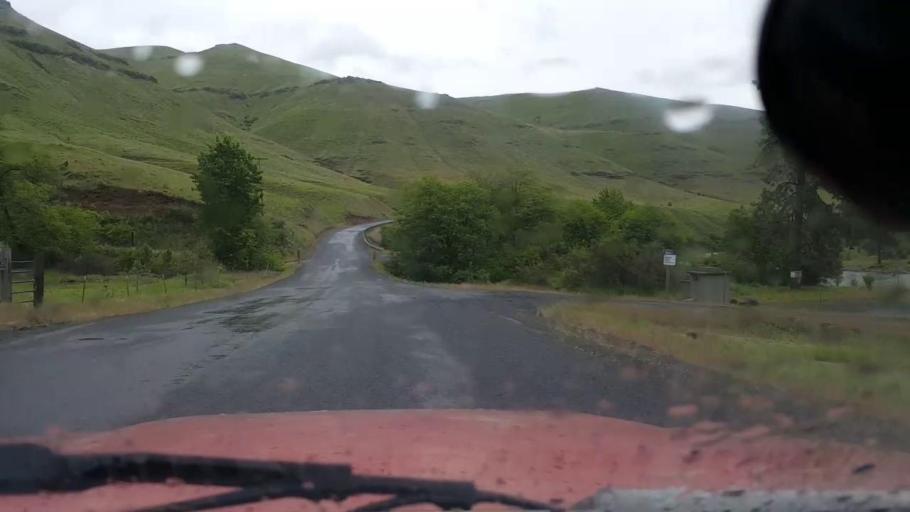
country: US
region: Washington
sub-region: Asotin County
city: Asotin
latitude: 46.0385
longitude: -117.2964
